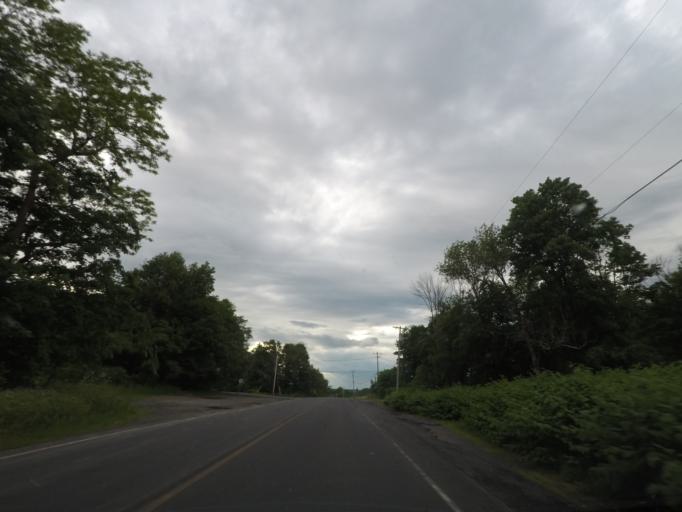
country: US
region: New York
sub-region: Dutchess County
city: Pine Plains
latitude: 41.9689
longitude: -73.5556
